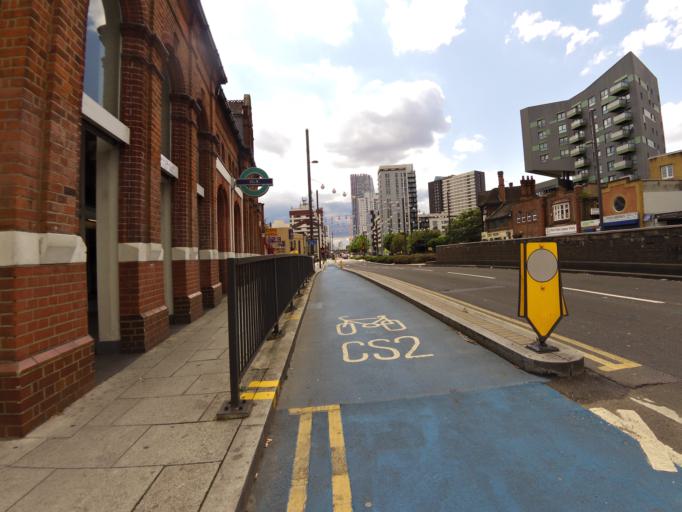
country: GB
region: England
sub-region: Greater London
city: Poplar
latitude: 51.5384
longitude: -0.0015
